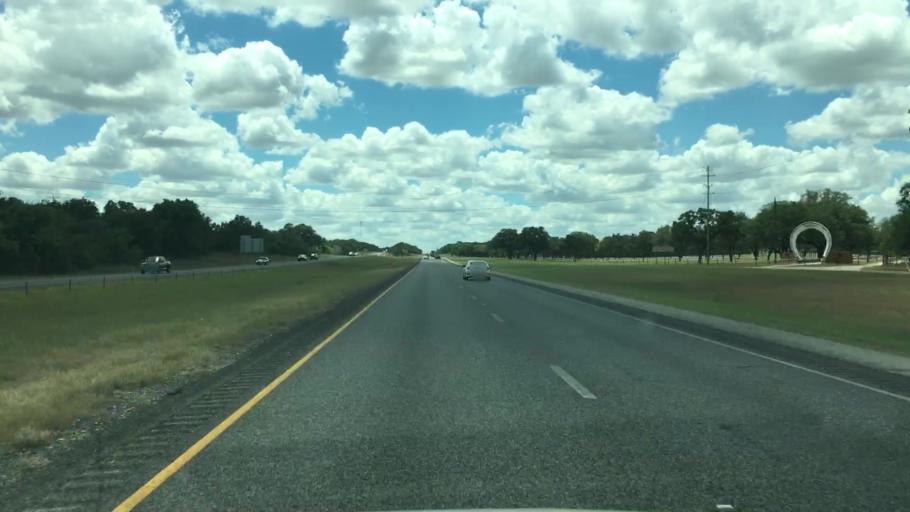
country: US
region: Texas
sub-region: Bexar County
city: Elmendorf
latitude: 29.2077
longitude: -98.4168
